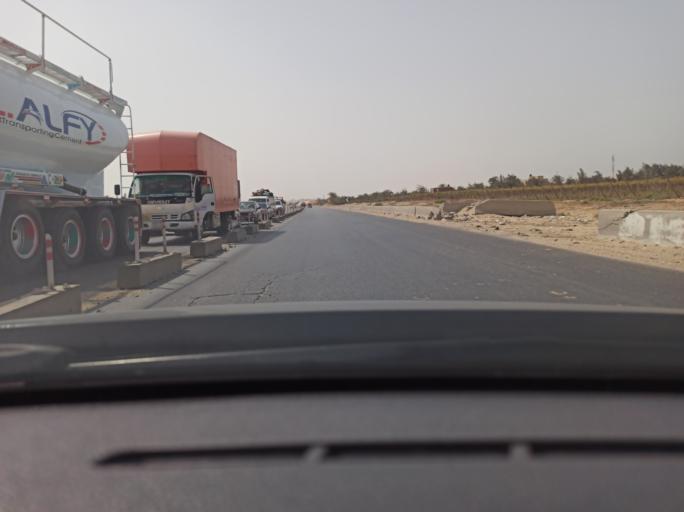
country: EG
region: Muhafazat al Fayyum
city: Al Wasitah
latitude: 29.2751
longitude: 31.2658
